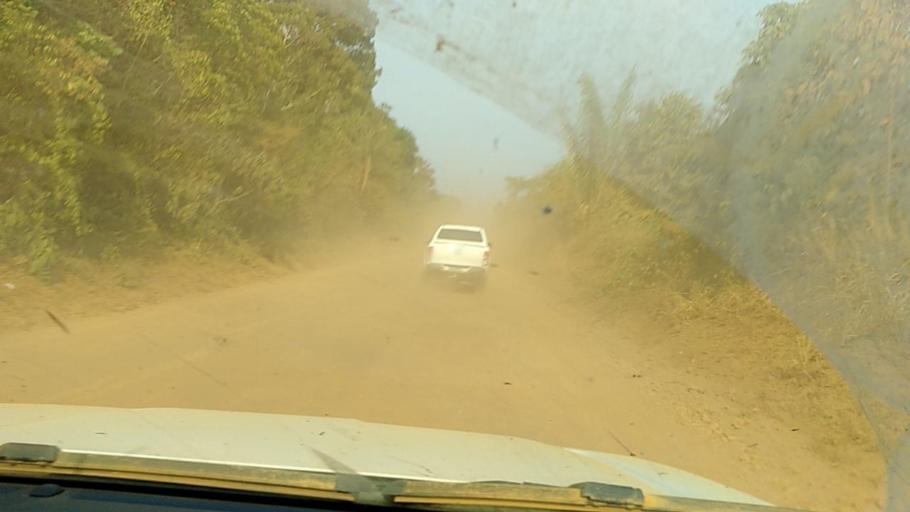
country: BR
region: Rondonia
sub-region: Porto Velho
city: Porto Velho
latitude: -8.7589
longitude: -63.9617
